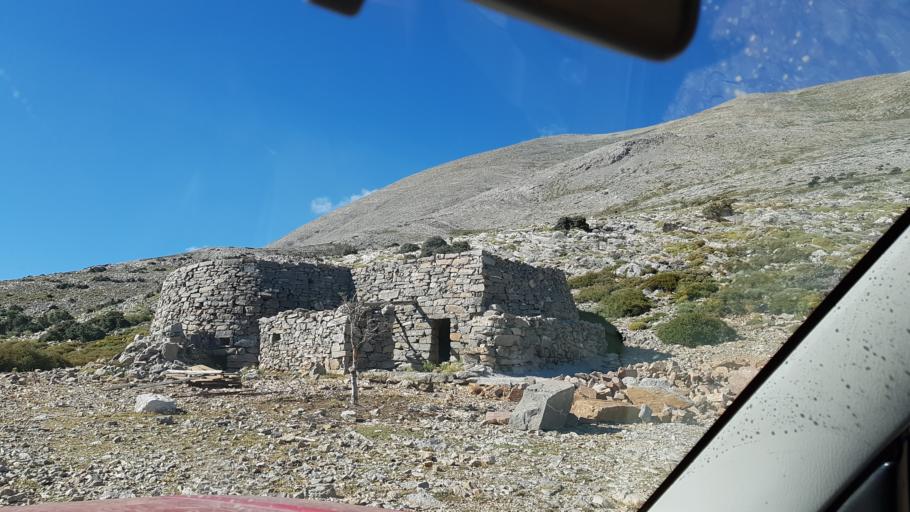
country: GR
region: Crete
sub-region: Nomos Rethymnis
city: Zoniana
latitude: 35.2104
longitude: 24.7566
